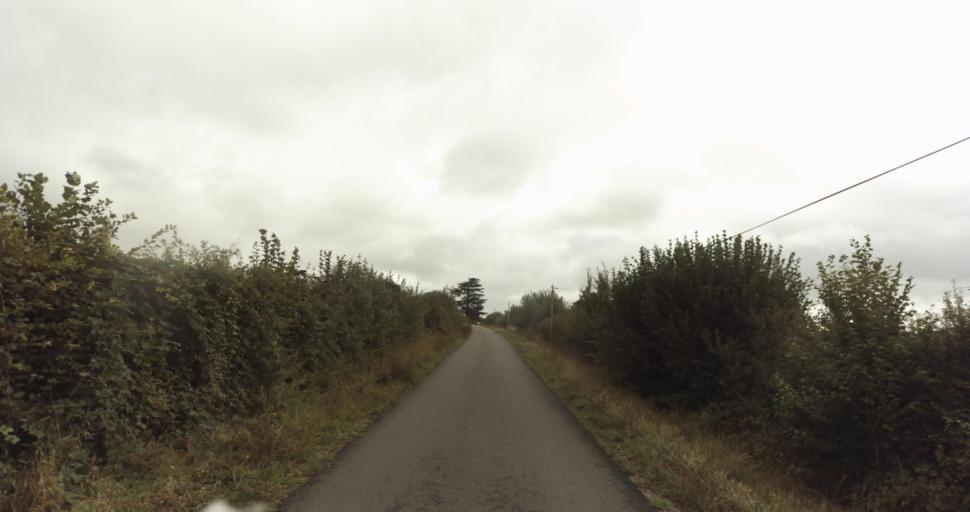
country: FR
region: Lower Normandy
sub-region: Departement de l'Orne
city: Gace
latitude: 48.8716
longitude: 0.2887
